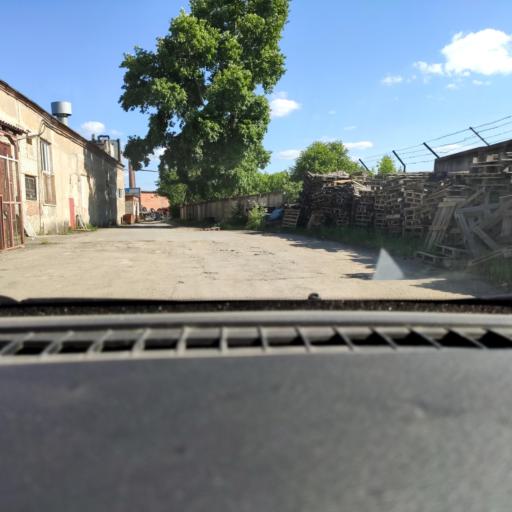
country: RU
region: Perm
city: Froly
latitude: 57.9517
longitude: 56.2544
